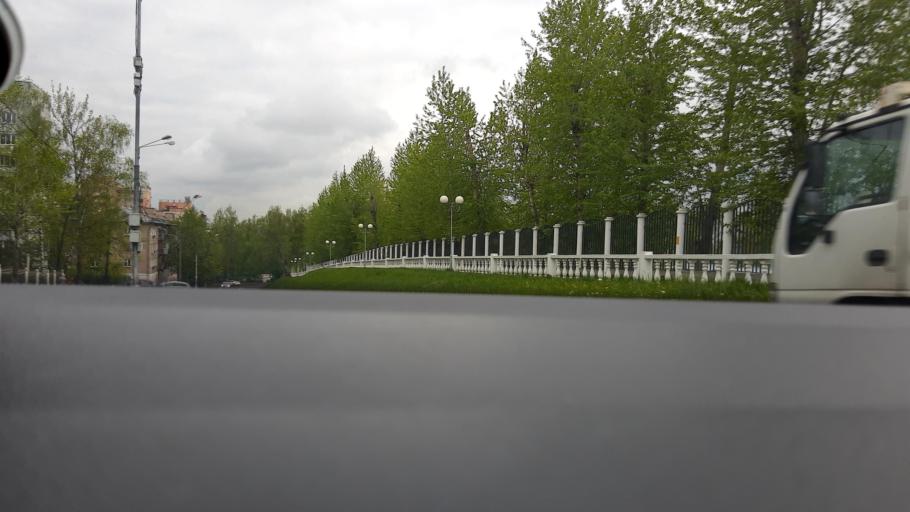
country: RU
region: Moskovskaya
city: Kotel'niki
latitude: 55.6282
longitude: 37.8481
